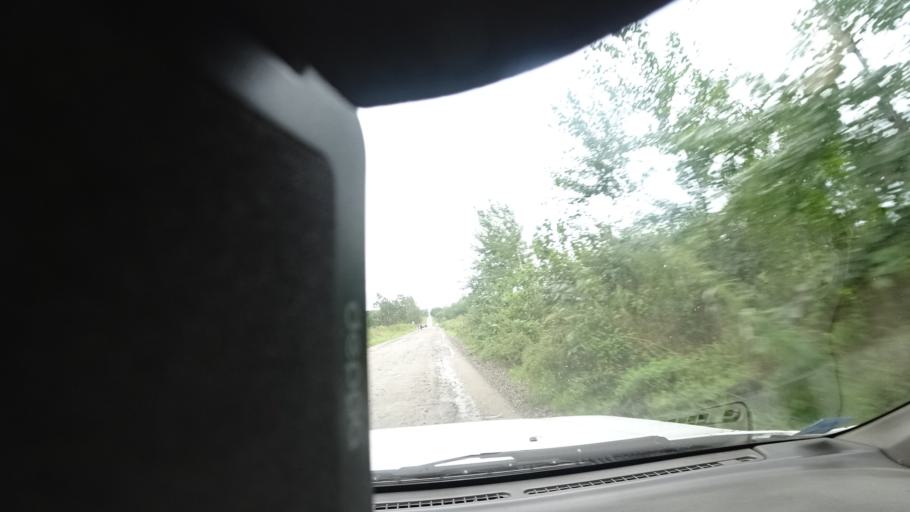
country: RU
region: Primorskiy
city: Lazo
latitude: 45.8700
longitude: 133.6880
